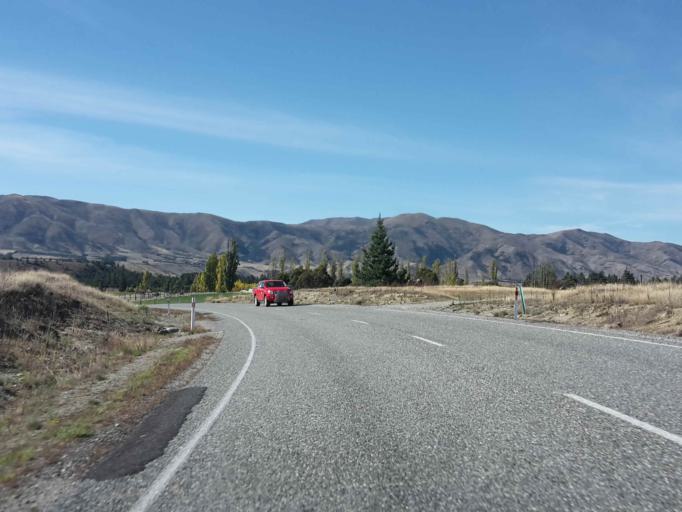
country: NZ
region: Otago
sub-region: Queenstown-Lakes District
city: Wanaka
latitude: -44.7346
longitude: 169.2632
